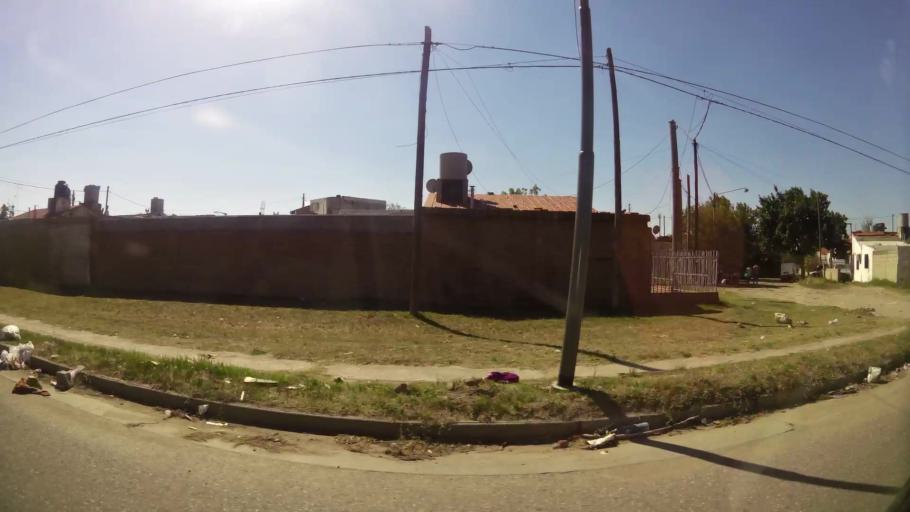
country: AR
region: Cordoba
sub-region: Departamento de Capital
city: Cordoba
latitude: -31.4157
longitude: -64.1442
